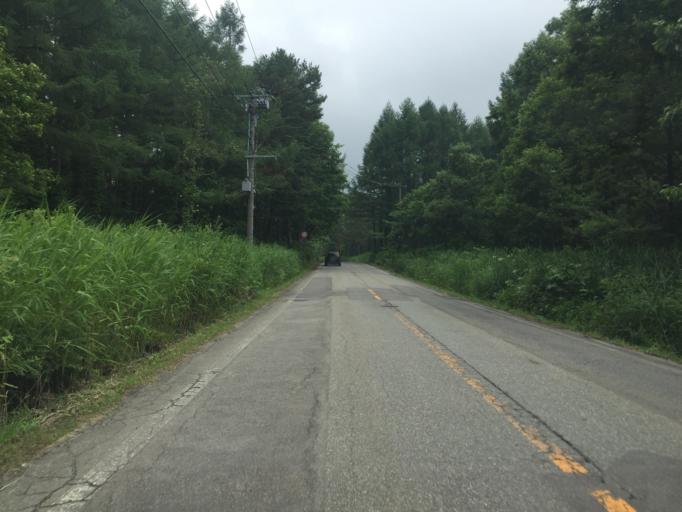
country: JP
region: Fukushima
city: Inawashiro
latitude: 37.6817
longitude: 140.0687
